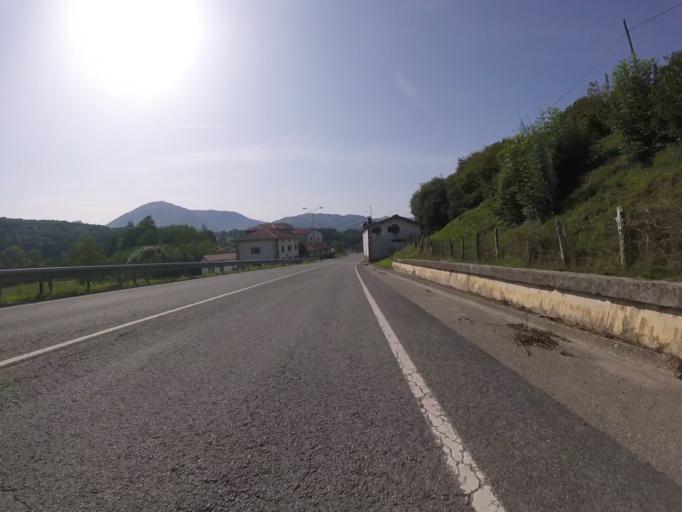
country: ES
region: Navarre
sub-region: Provincia de Navarra
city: Zugarramurdi
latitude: 43.1977
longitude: -1.4839
